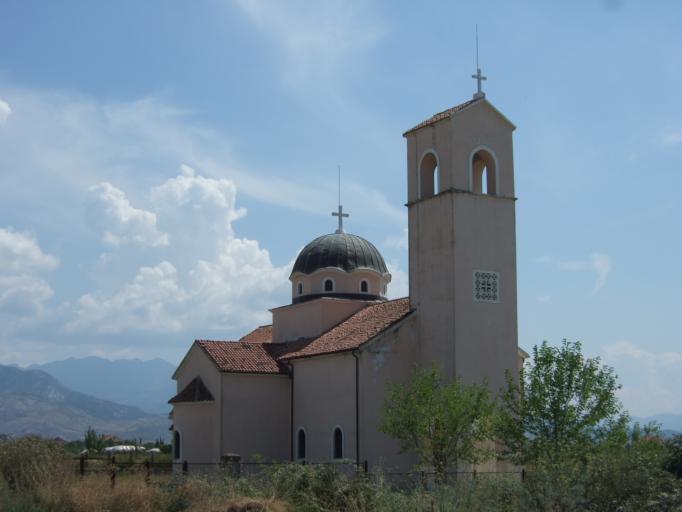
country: AL
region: Shkoder
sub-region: Rrethi i Malesia e Madhe
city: Grude-Fushe
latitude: 42.1332
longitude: 19.4888
